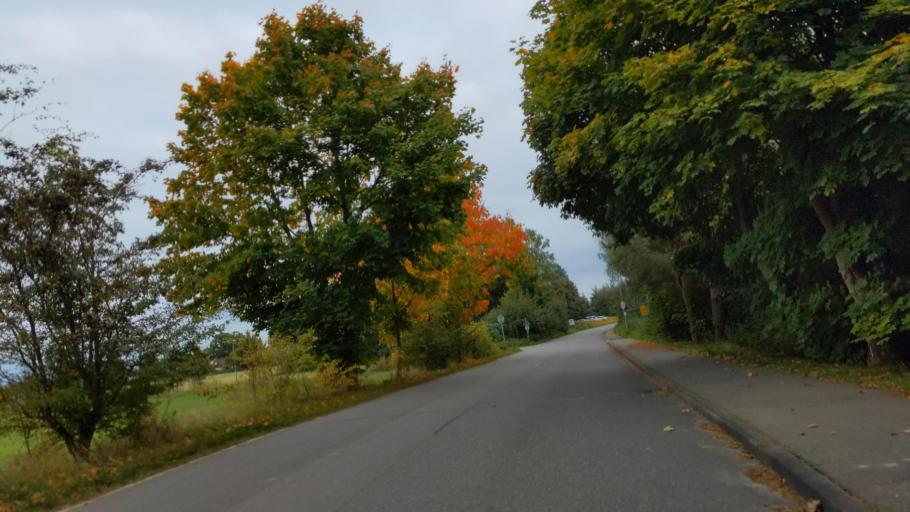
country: DE
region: Schleswig-Holstein
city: Sierksdorf
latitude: 54.0617
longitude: 10.7563
